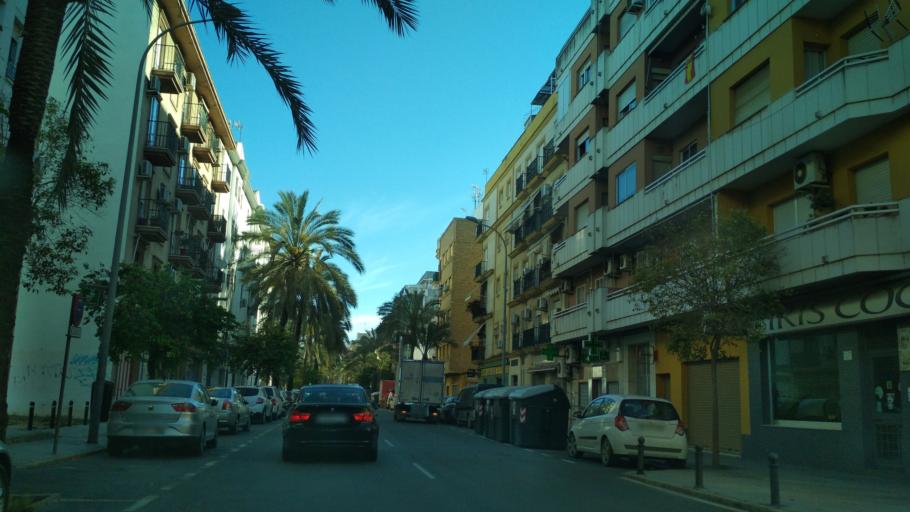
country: ES
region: Andalusia
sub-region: Provincia de Huelva
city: Huelva
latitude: 37.2696
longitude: -6.9511
